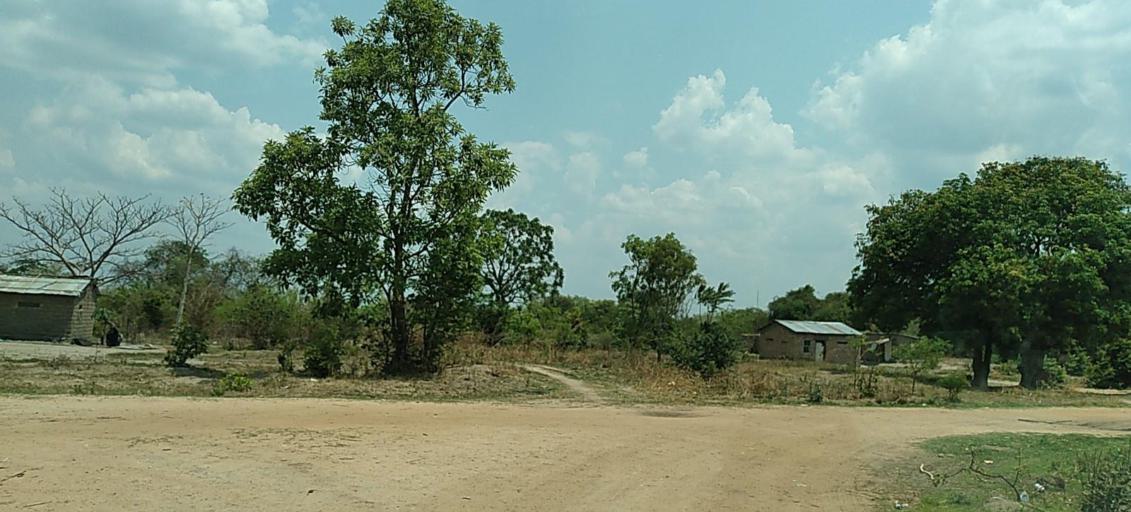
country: ZM
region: Copperbelt
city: Luanshya
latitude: -13.1550
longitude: 28.3147
